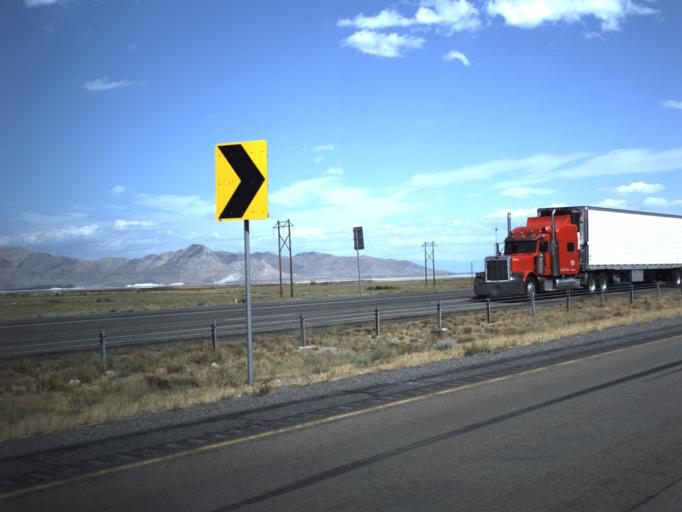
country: US
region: Utah
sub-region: Tooele County
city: Grantsville
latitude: 40.7442
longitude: -112.6366
